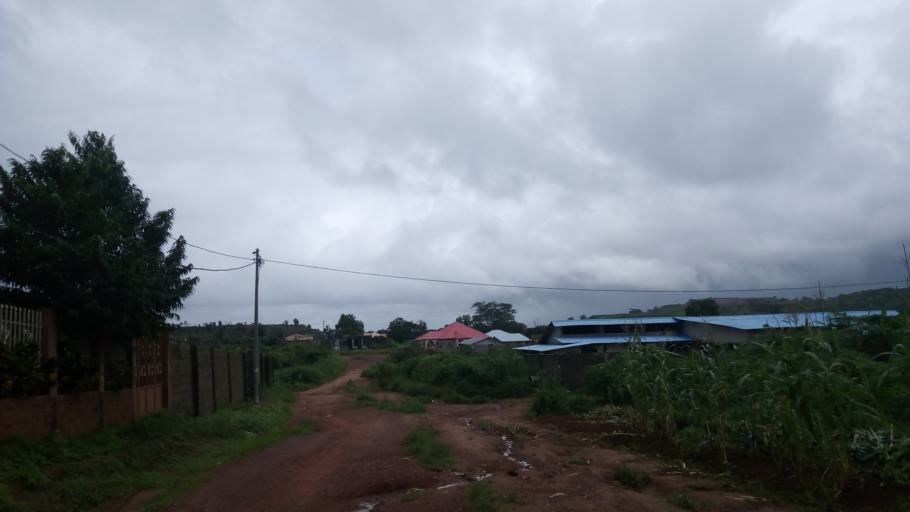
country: SL
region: Northern Province
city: Lunsar
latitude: 8.6909
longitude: -12.5288
